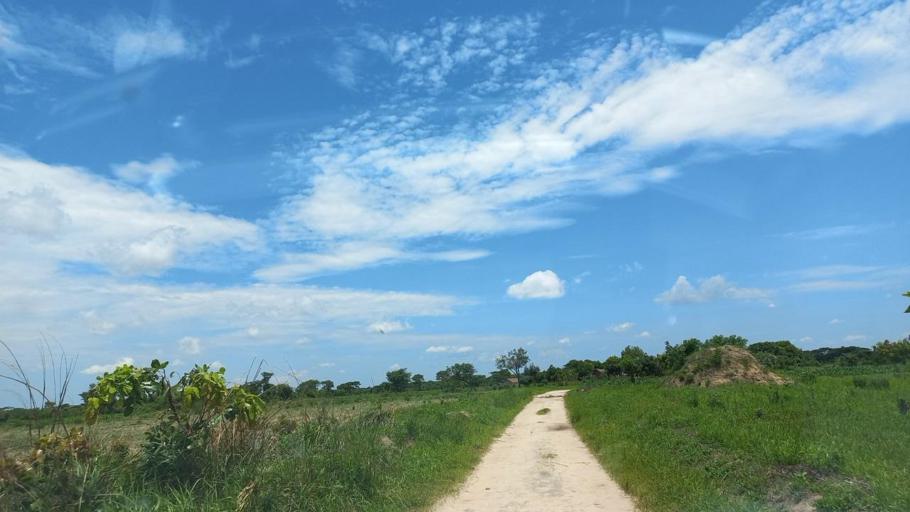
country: ZM
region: Copperbelt
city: Ndola
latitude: -12.8679
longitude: 28.4383
